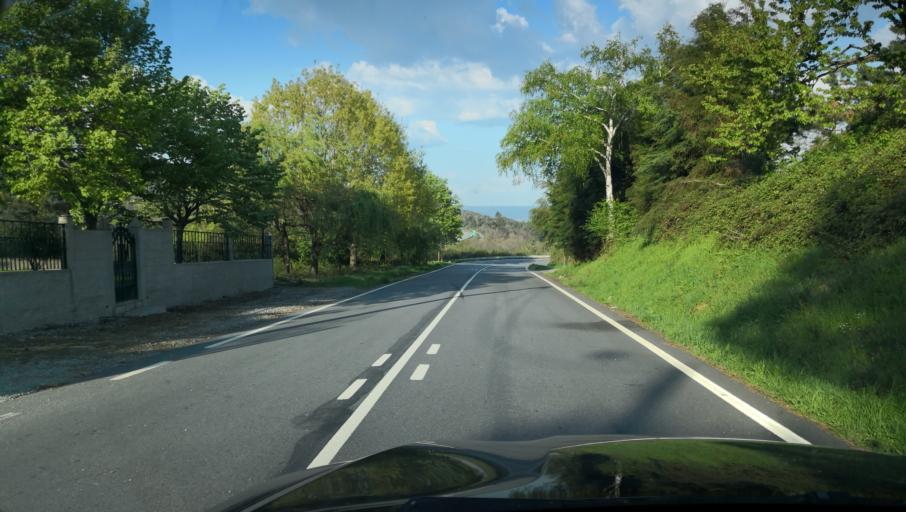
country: PT
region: Vila Real
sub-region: Santa Marta de Penaguiao
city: Santa Marta de Penaguiao
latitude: 41.2822
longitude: -7.8292
